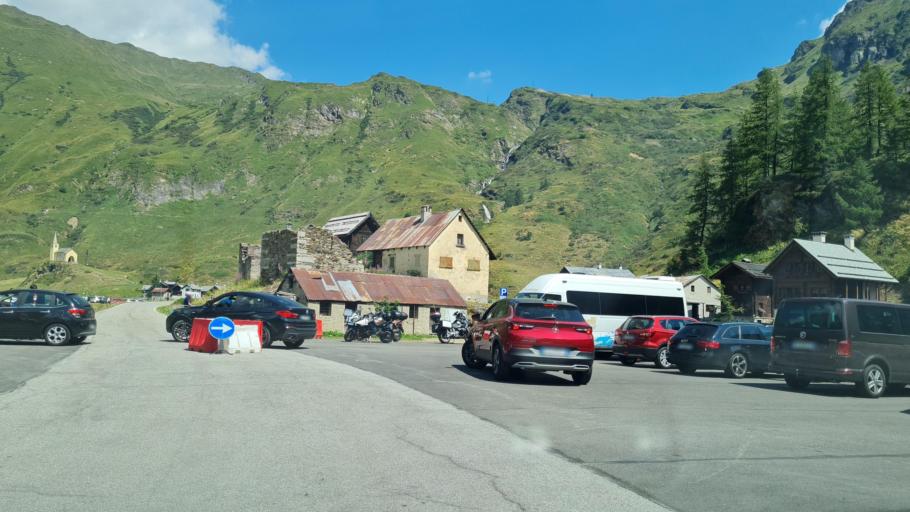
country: IT
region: Piedmont
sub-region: Provincia Verbano-Cusio-Ossola
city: Formazza
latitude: 46.4196
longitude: 8.4165
